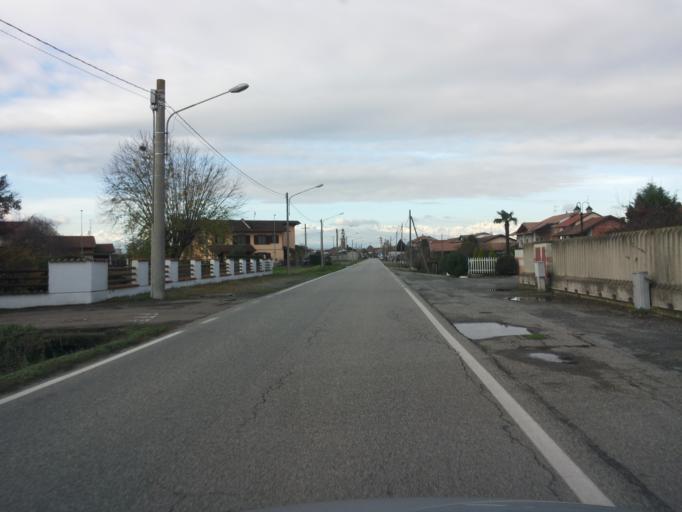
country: IT
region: Piedmont
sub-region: Provincia di Vercelli
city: Tronzano Vercellese
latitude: 45.3359
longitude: 8.1823
